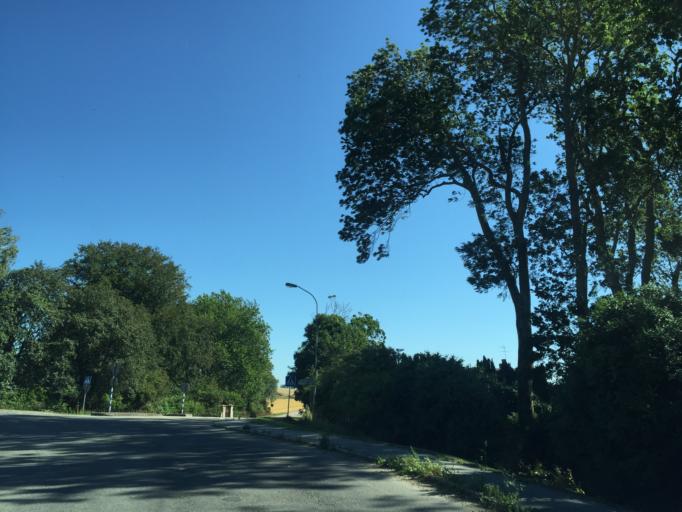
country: SE
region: Skane
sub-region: Ystads Kommun
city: Kopingebro
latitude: 55.4435
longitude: 14.1214
